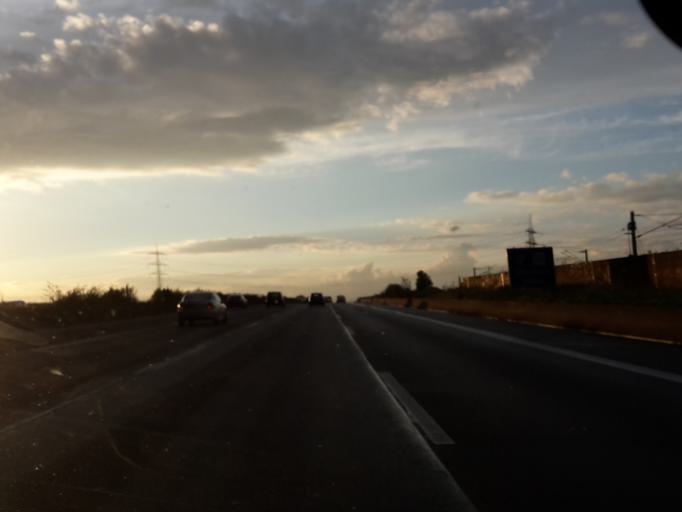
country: DE
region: Hesse
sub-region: Regierungsbezirk Darmstadt
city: Florsheim
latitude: 50.0400
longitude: 8.4217
